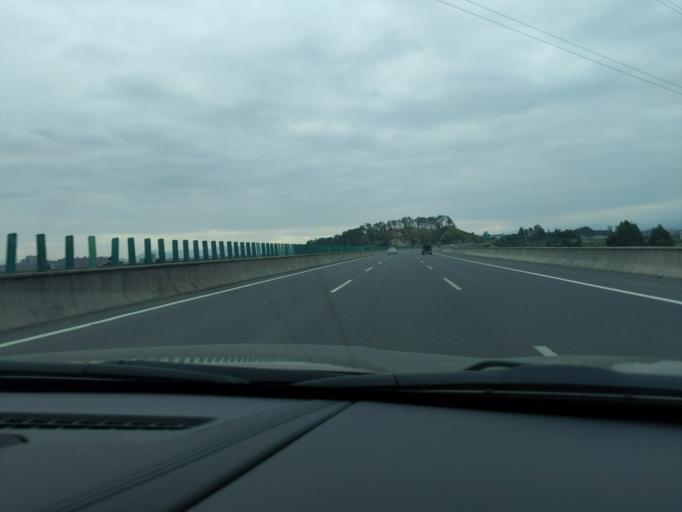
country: CN
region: Fujian
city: Neikeng
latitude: 24.7839
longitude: 118.4914
